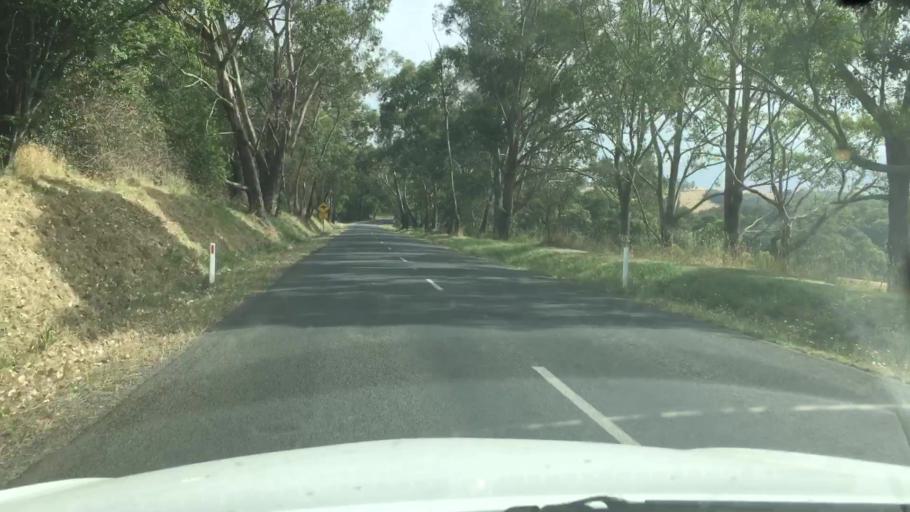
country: AU
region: Victoria
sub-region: Yarra Ranges
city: Macclesfield
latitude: -37.8826
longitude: 145.4768
